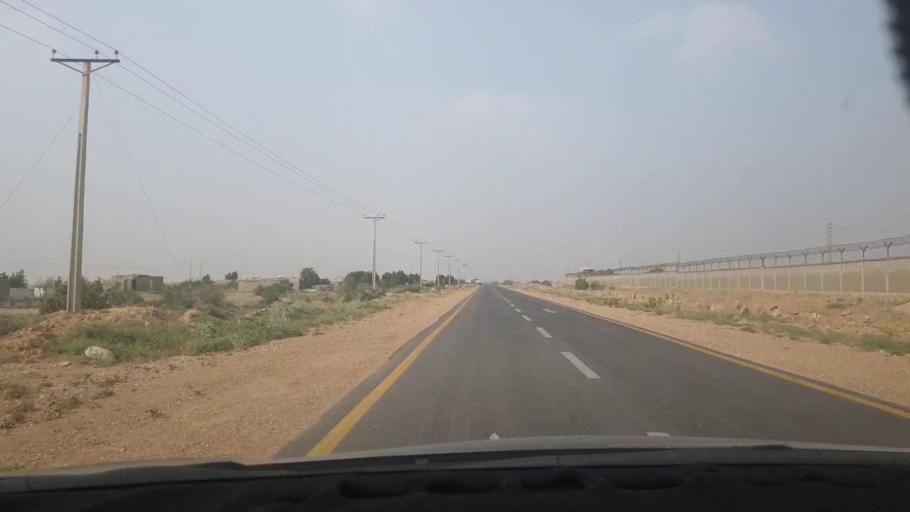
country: PK
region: Sindh
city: Jamshoro
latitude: 25.5628
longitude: 68.3178
